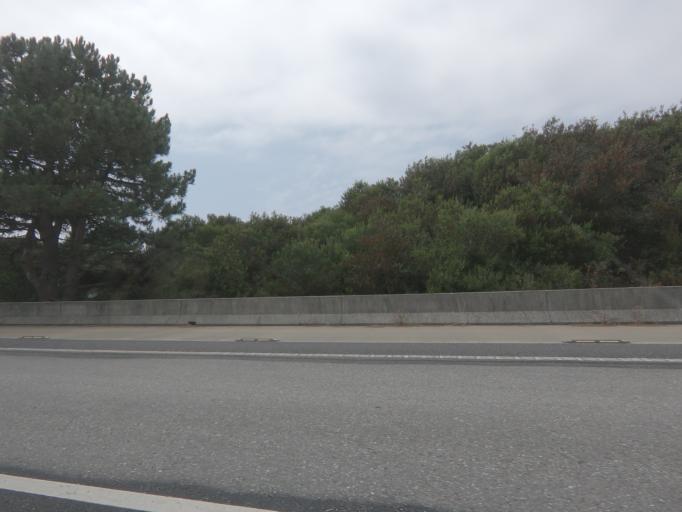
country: ES
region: Galicia
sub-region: Provincia de Pontevedra
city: Oia
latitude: 41.9809
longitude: -8.8846
